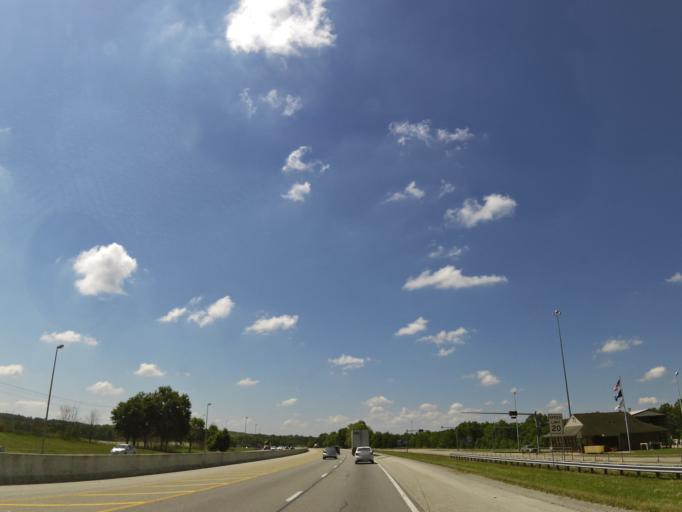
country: US
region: Kentucky
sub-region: Laurel County
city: London
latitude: 37.0483
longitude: -84.0990
